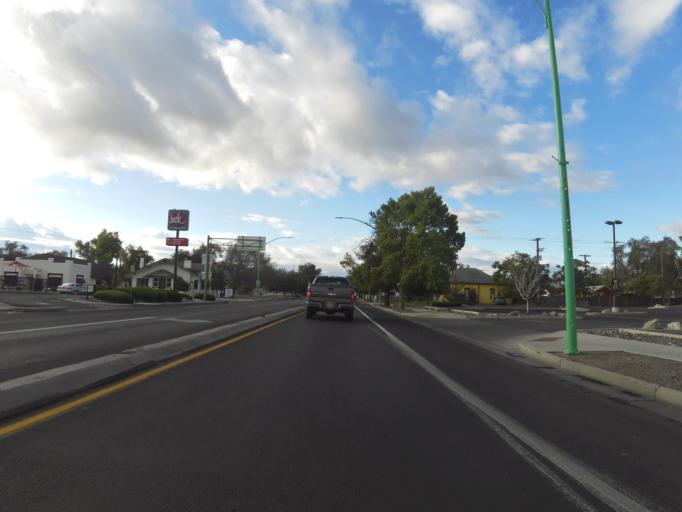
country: US
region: Nevada
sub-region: Churchill County
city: Fallon
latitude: 39.4746
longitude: -118.7817
